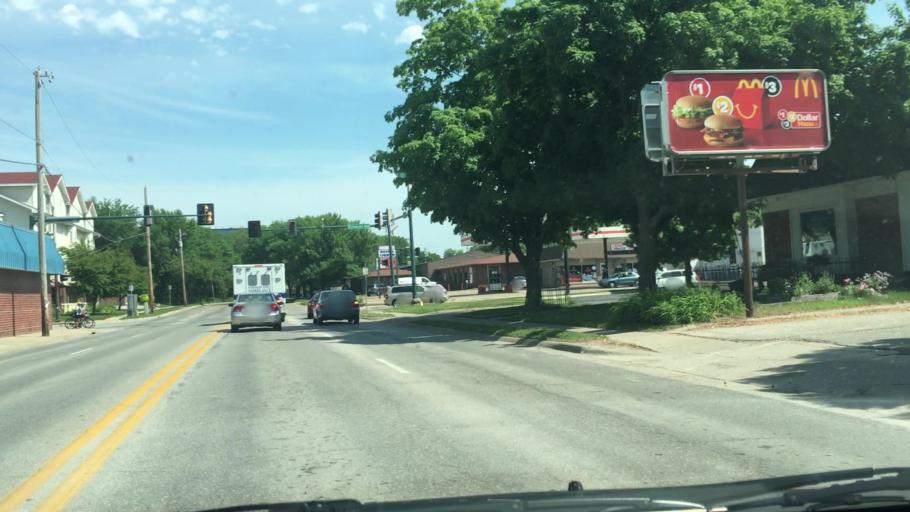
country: US
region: Iowa
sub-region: Johnson County
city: Iowa City
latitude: 41.6489
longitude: -91.5320
